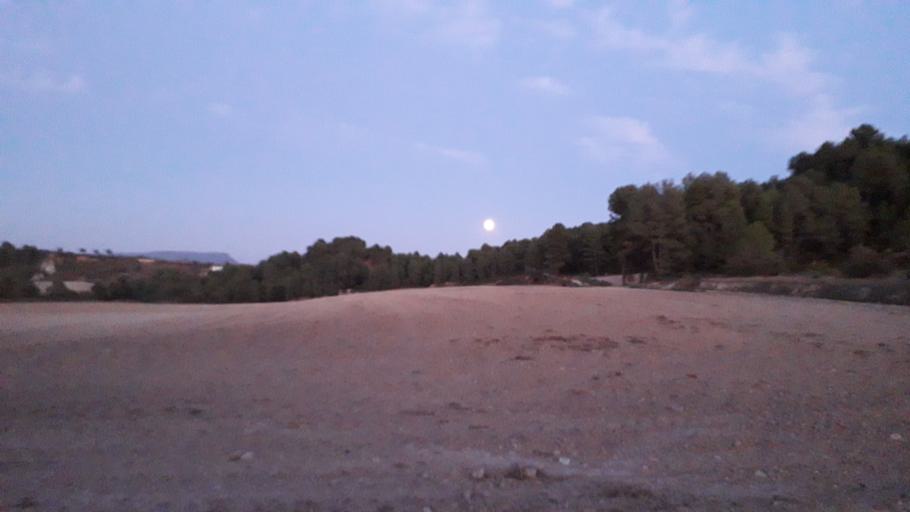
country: ES
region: Catalonia
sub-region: Provincia de Barcelona
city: Jorba
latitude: 41.5718
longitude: 1.5758
